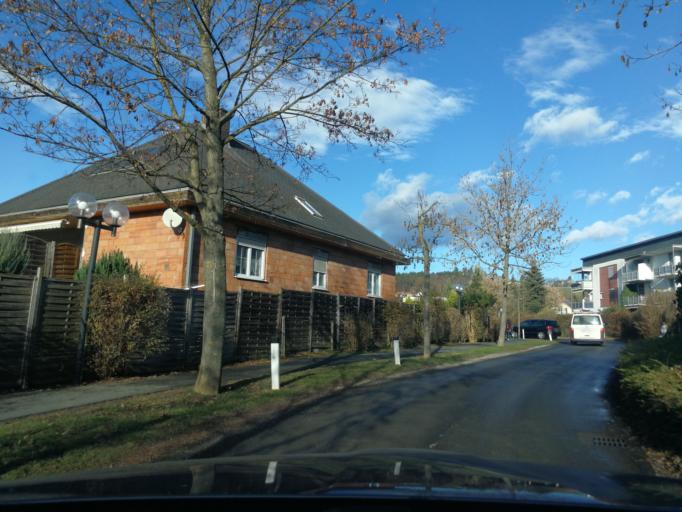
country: AT
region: Styria
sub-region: Politischer Bezirk Weiz
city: Gleisdorf
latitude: 47.1031
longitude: 15.7171
